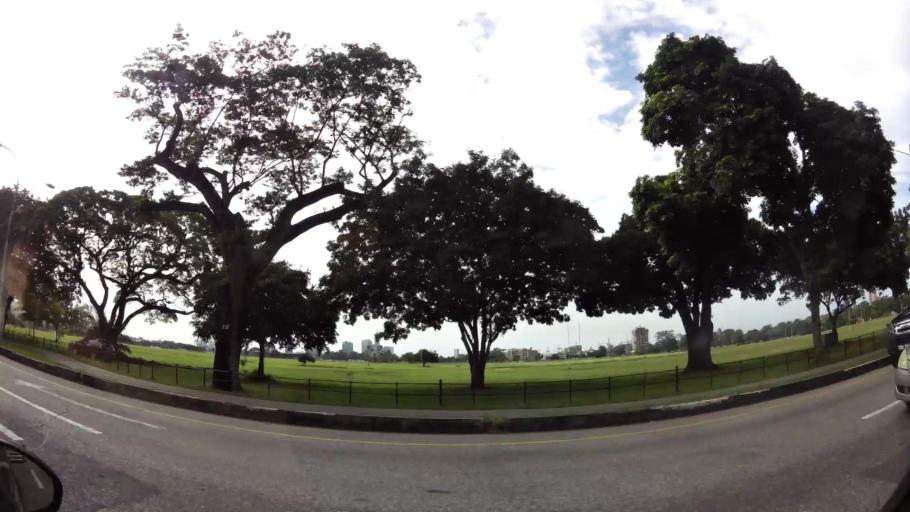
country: TT
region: City of Port of Spain
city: Port-of-Spain
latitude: 10.6734
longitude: -61.5140
